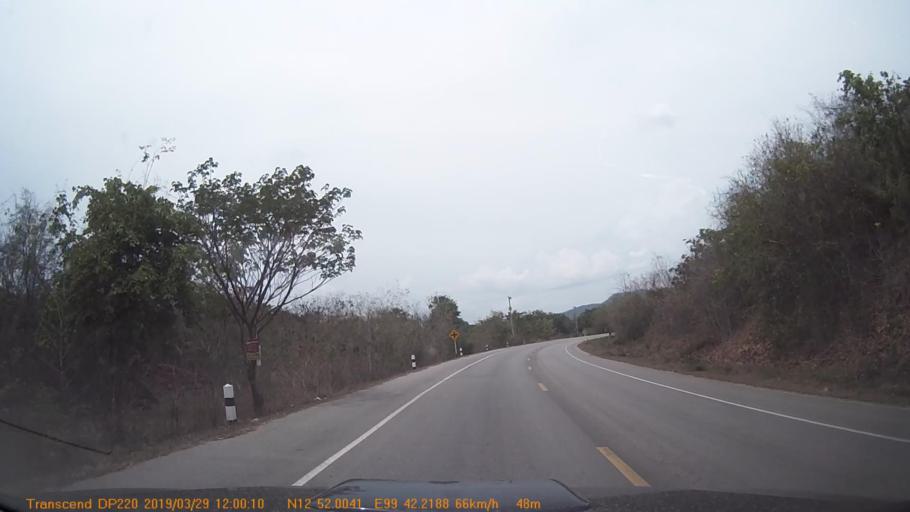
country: TH
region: Phetchaburi
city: Kaeng Krachan
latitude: 12.8665
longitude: 99.7033
